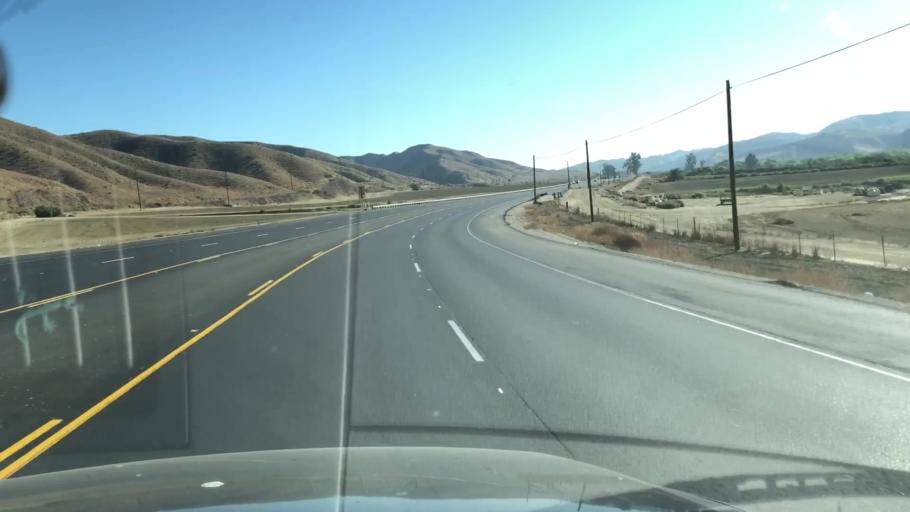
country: US
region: California
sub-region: Los Angeles County
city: Val Verde
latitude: 34.4053
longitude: -118.7020
